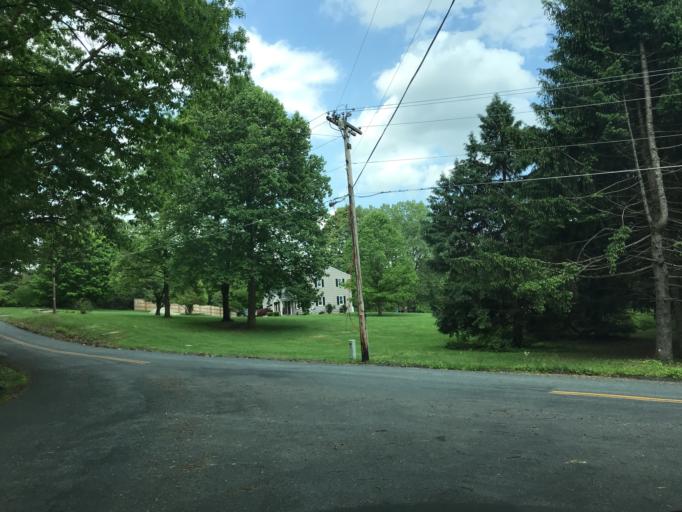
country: US
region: Pennsylvania
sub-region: York County
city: Susquehanna Trails
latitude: 39.6892
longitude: -76.3547
